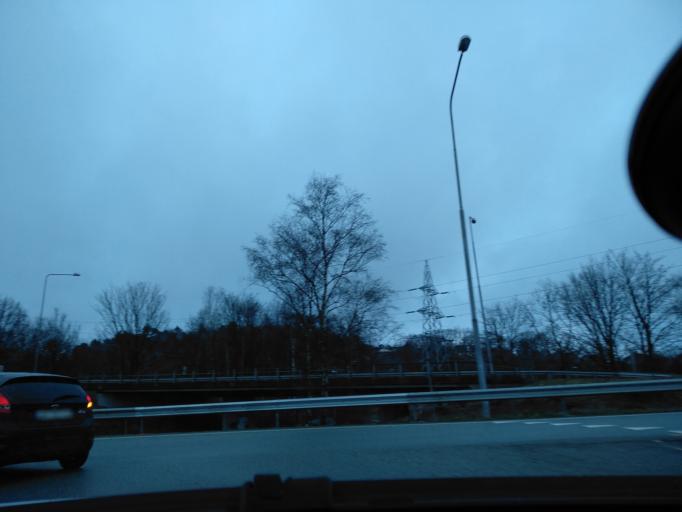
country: NO
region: Rogaland
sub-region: Stavanger
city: Stavanger
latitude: 58.9221
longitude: 5.7076
